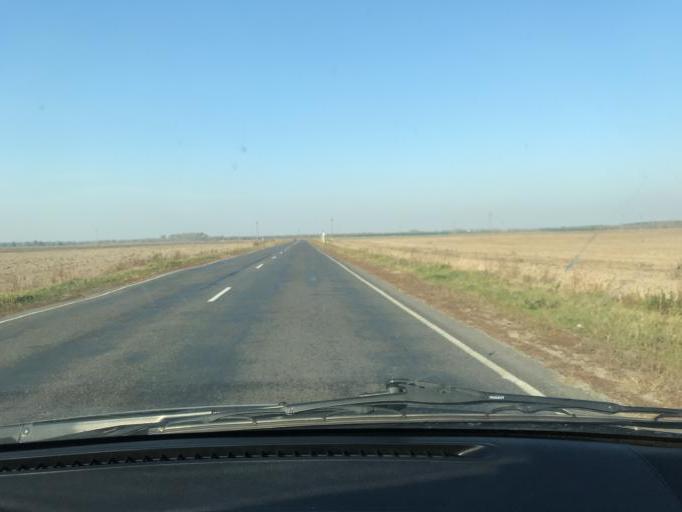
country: BY
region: Brest
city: Davyd-Haradok
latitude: 52.0607
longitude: 27.2554
